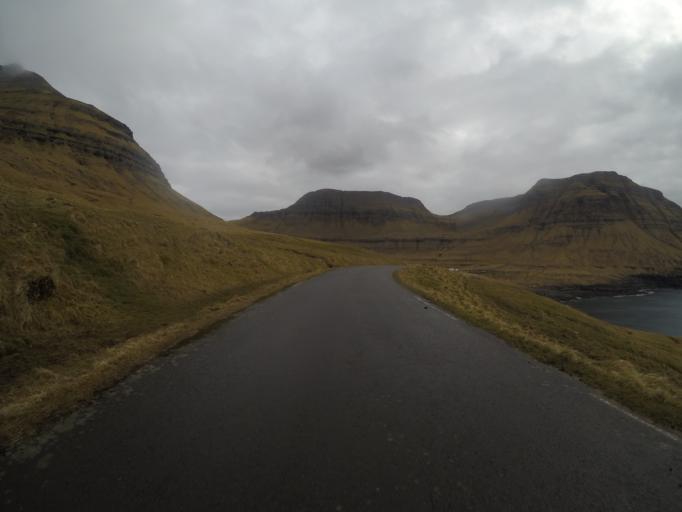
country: FO
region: Streymoy
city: Kollafjordhur
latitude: 62.0411
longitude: -6.9454
